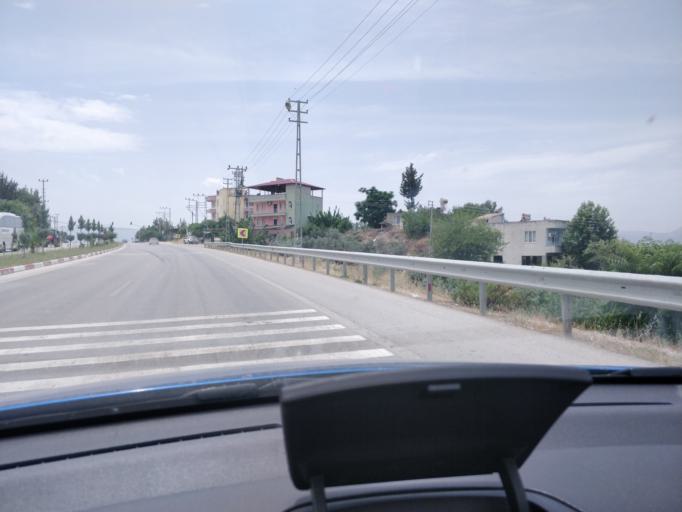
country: TR
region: Mersin
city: Mut
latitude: 36.6187
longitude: 33.4416
